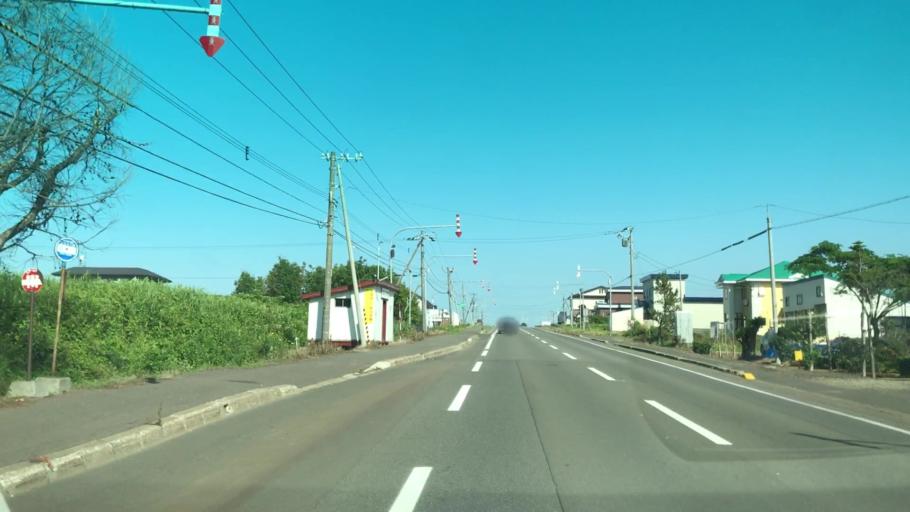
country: JP
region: Hokkaido
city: Iwanai
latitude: 42.9837
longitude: 140.5627
